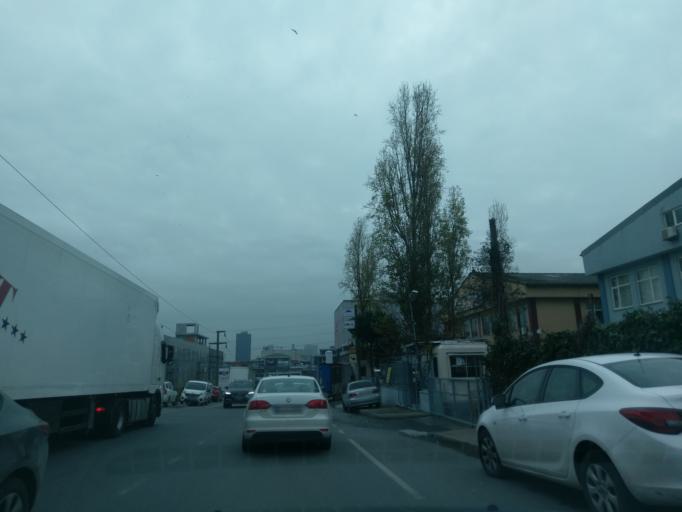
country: TR
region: Istanbul
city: Basaksehir
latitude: 41.0727
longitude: 28.8125
